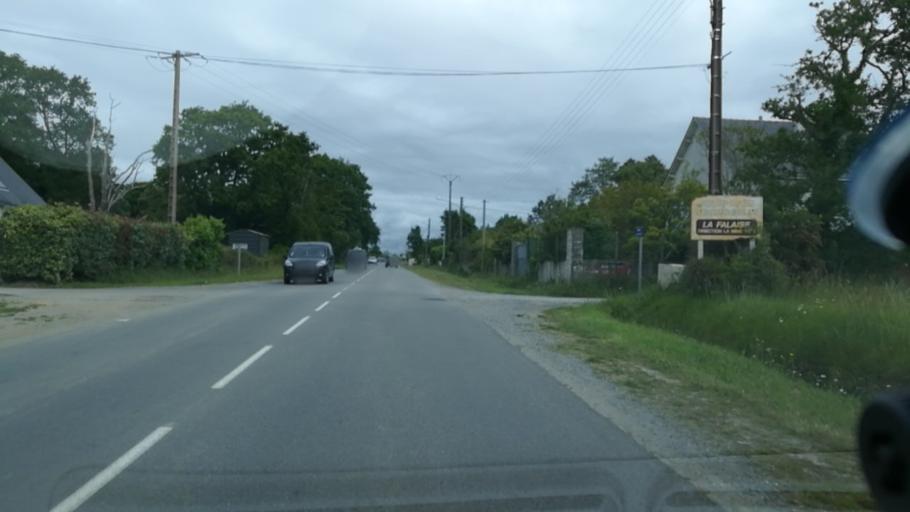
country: FR
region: Brittany
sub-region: Departement du Morbihan
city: Penestin
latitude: 47.4742
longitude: -2.4788
